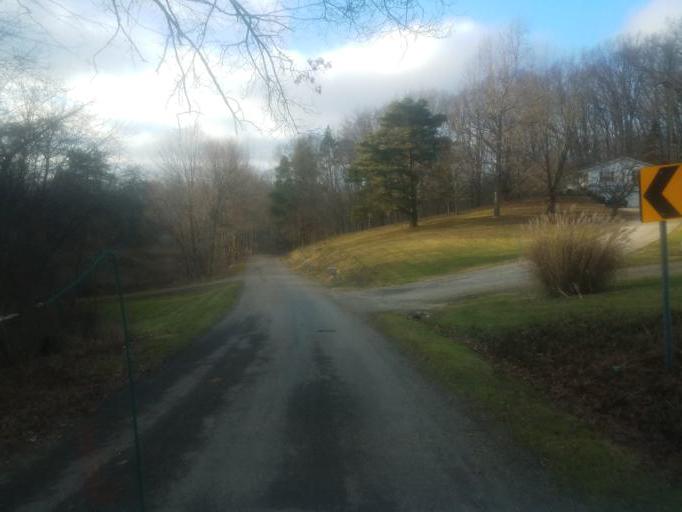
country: US
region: Ohio
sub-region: Sandusky County
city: Bellville
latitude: 40.6229
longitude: -82.3724
